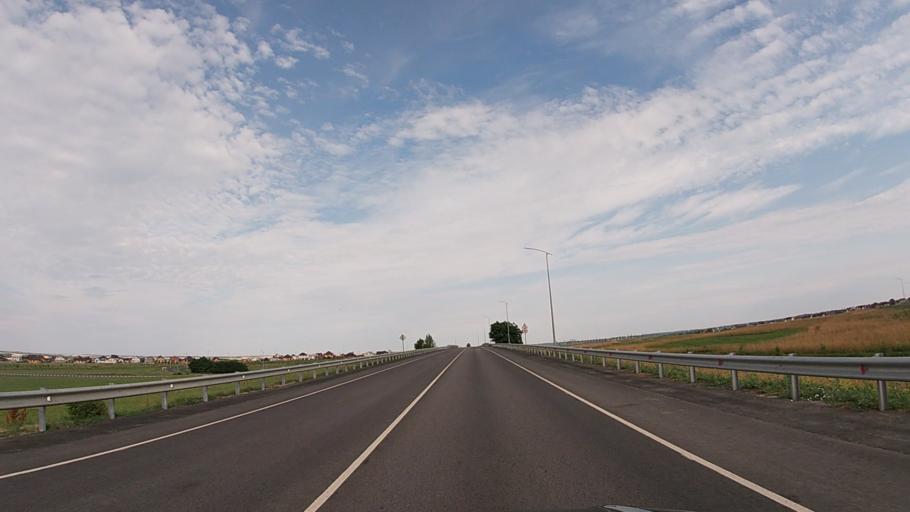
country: RU
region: Belgorod
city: Severnyy
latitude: 50.6741
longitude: 36.4753
